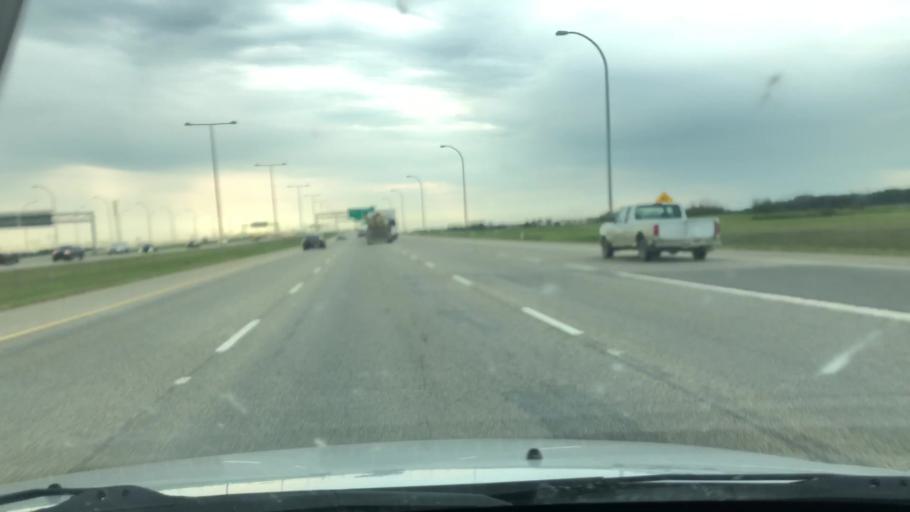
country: CA
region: Alberta
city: Beaumont
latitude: 53.4377
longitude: -113.4690
